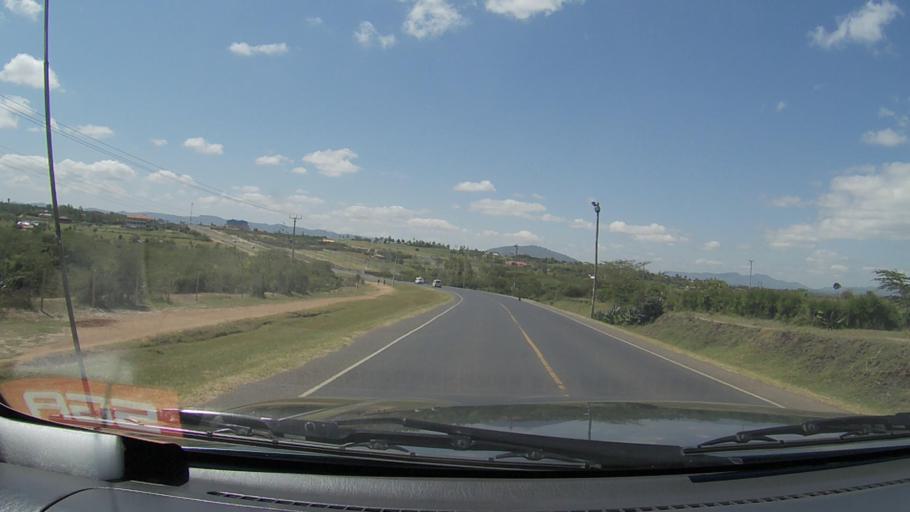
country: KE
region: Machakos
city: Machakos
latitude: -1.5344
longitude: 37.1929
